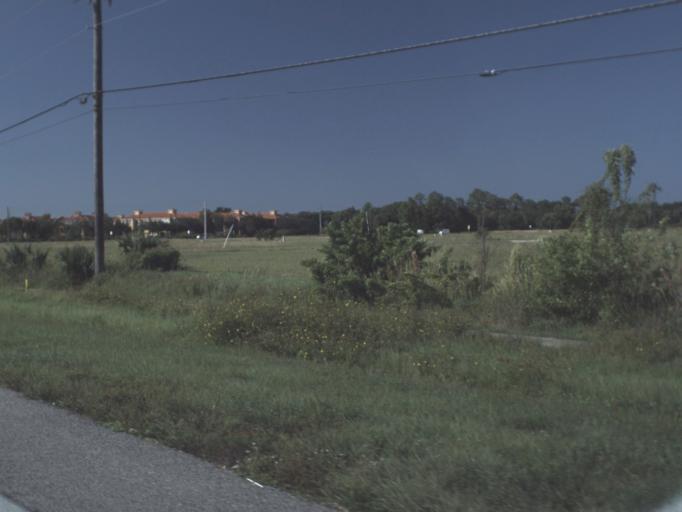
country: US
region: Florida
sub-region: Lee County
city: Estero
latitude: 26.4005
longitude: -81.8108
